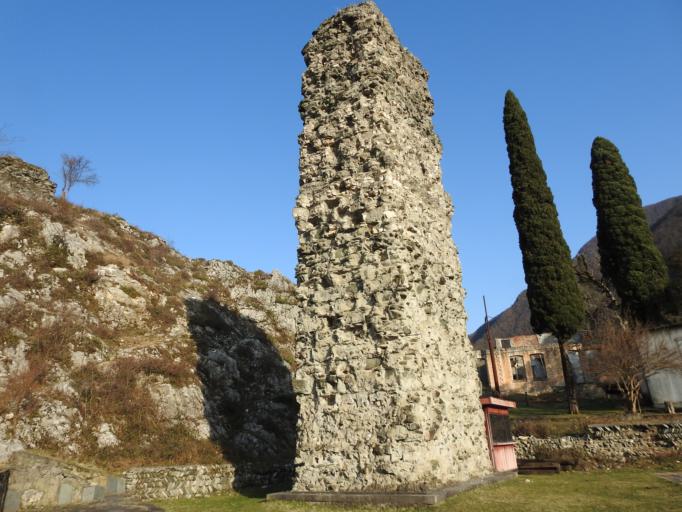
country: GE
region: Abkhazia
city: Bich'vinta
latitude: 43.2399
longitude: 40.3971
